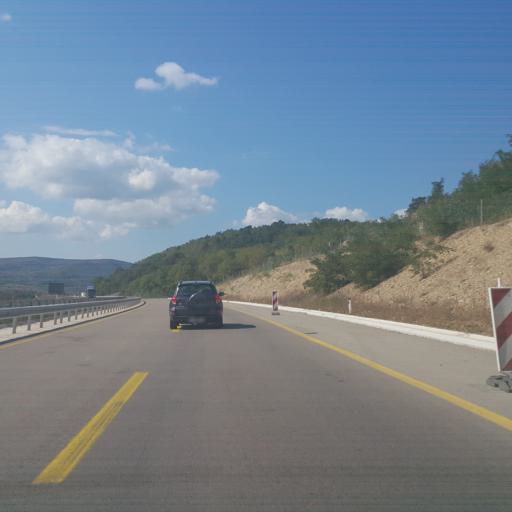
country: RS
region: Central Serbia
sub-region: Pirotski Okrug
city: Bela Palanka
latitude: 43.2362
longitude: 22.3049
